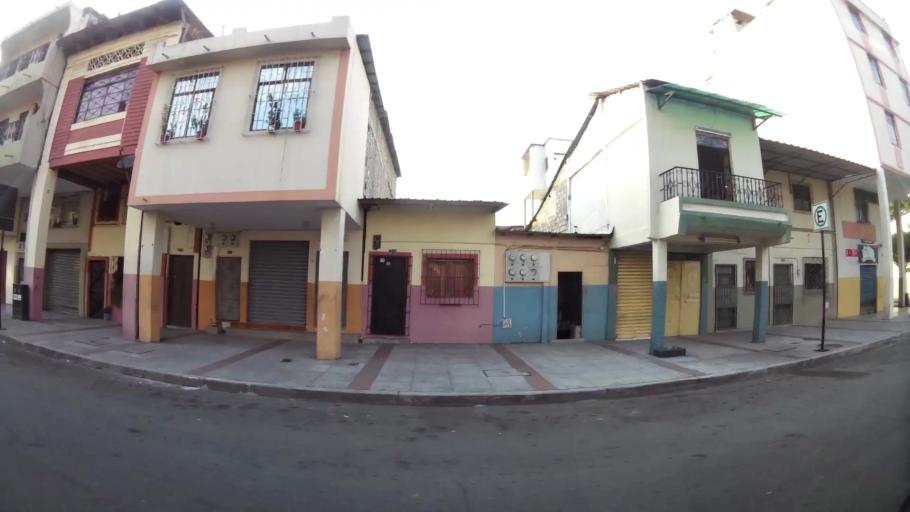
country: EC
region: Guayas
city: Guayaquil
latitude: -2.2088
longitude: -79.9004
